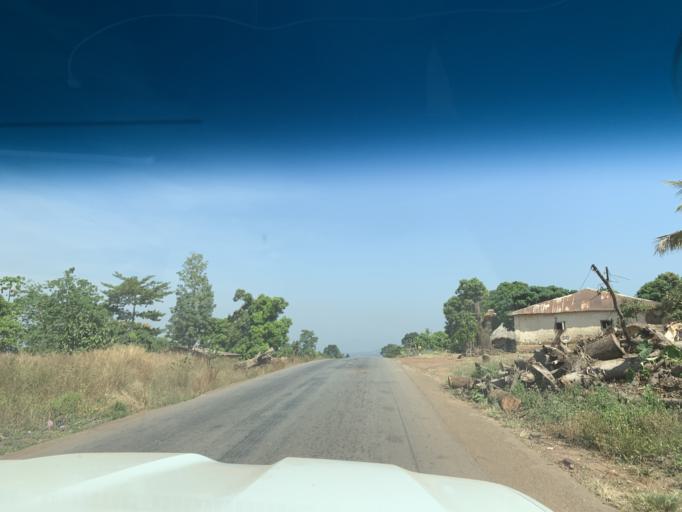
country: GN
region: Kindia
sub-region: Kindia
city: Kindia
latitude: 10.0690
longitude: -12.6532
